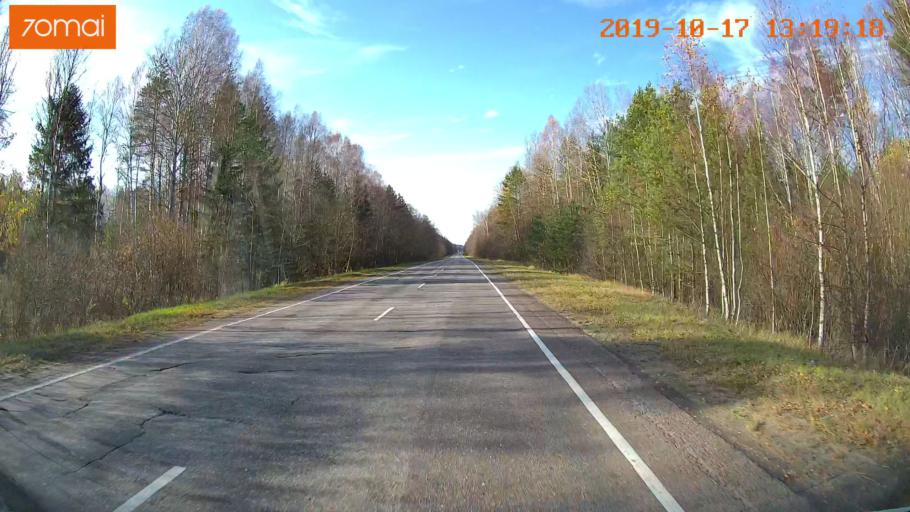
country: RU
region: Rjazan
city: Gus'-Zheleznyy
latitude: 55.0685
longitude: 41.0775
